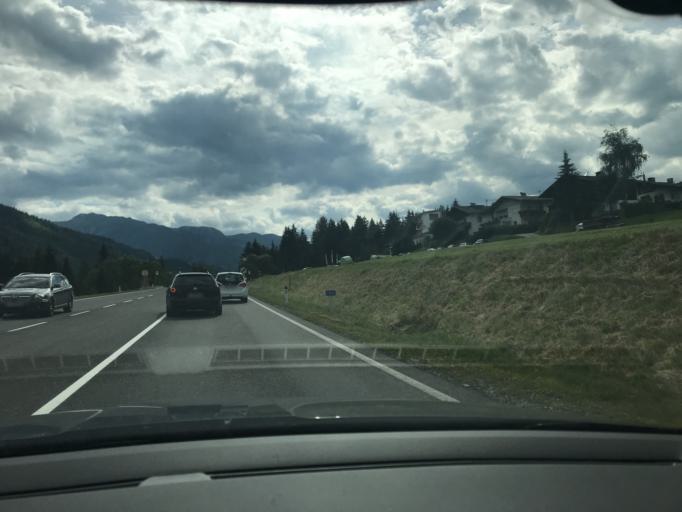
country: AT
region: Tyrol
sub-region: Politischer Bezirk Lienz
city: Strassen
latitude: 46.7532
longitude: 12.5080
